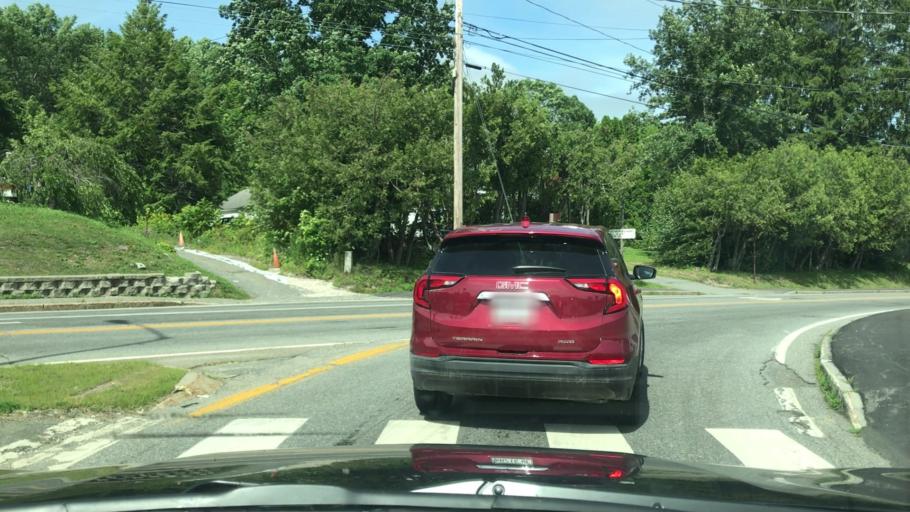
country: US
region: Maine
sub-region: Hancock County
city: Bucksport
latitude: 44.5710
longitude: -68.7874
